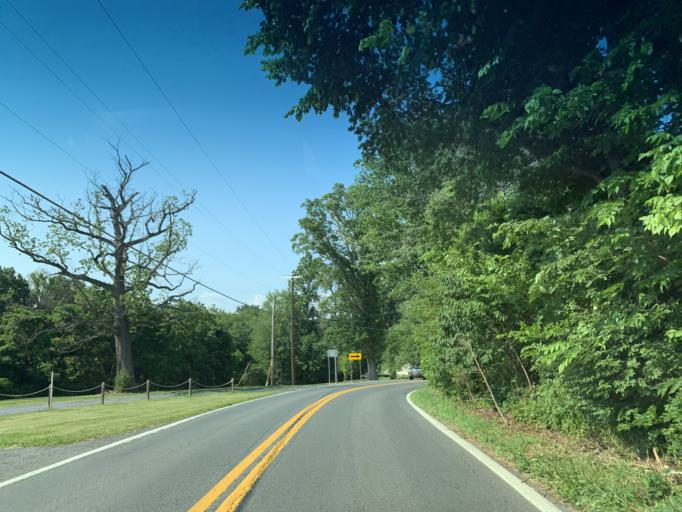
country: US
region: Maryland
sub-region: Montgomery County
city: Poolesville
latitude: 39.1997
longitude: -77.3950
